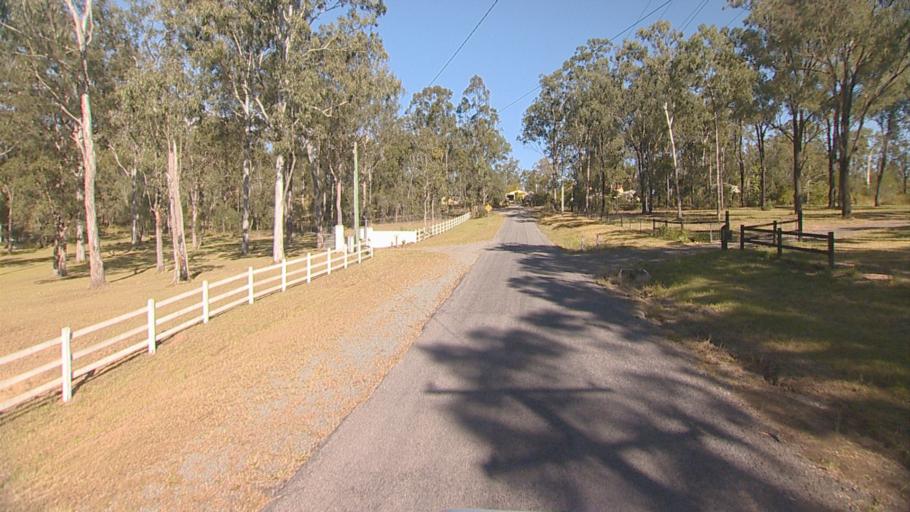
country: AU
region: Queensland
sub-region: Logan
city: Chambers Flat
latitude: -27.8196
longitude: 153.0767
